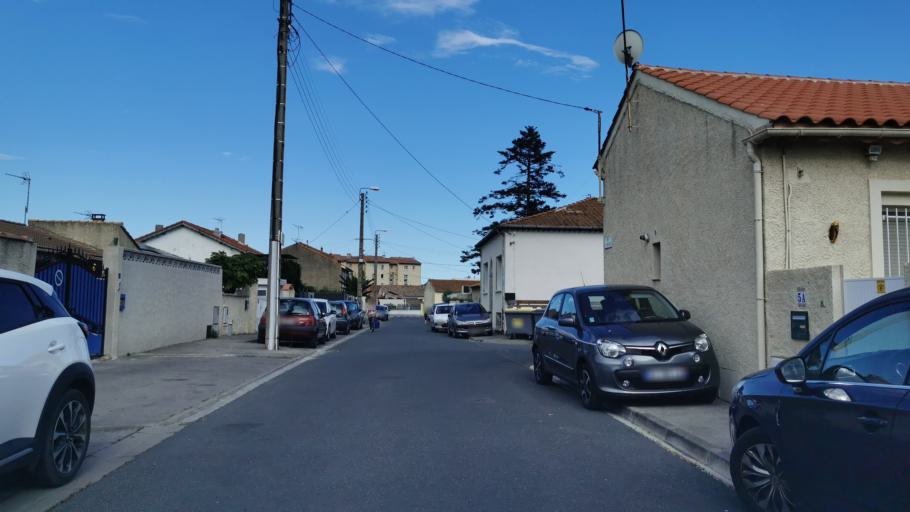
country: FR
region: Languedoc-Roussillon
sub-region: Departement de l'Aude
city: Narbonne
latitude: 43.1838
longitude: 2.9922
